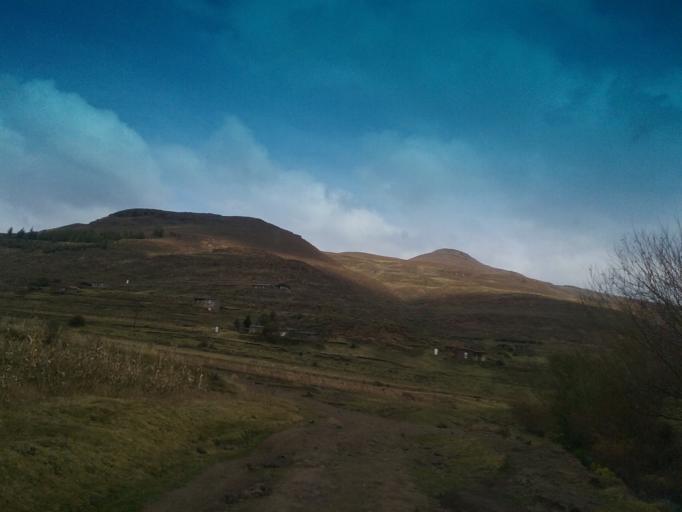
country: LS
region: Quthing
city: Quthing
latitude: -30.1812
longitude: 28.0329
